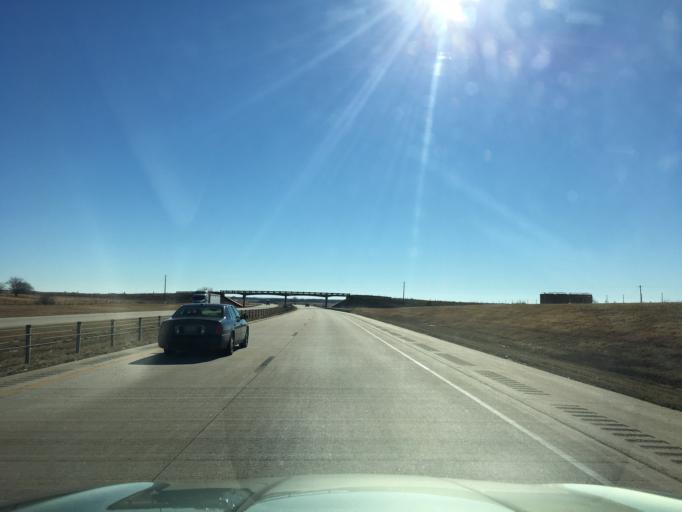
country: US
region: Oklahoma
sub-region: Kay County
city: Tonkawa
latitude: 36.5092
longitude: -97.3370
